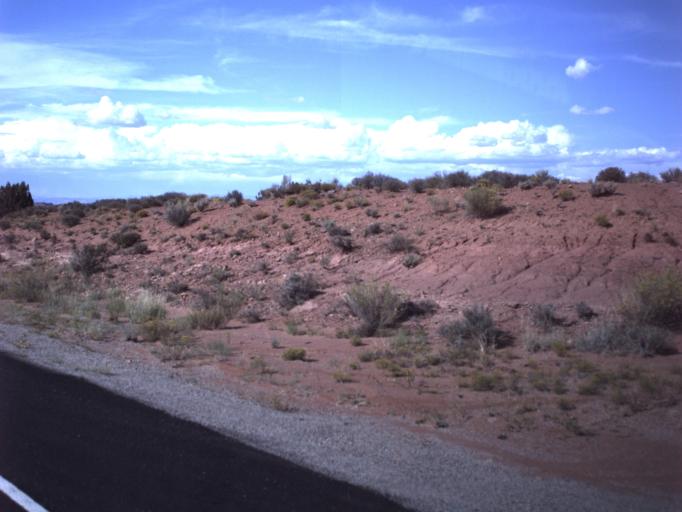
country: US
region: Utah
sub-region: Grand County
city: Moab
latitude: 38.6027
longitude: -109.8165
